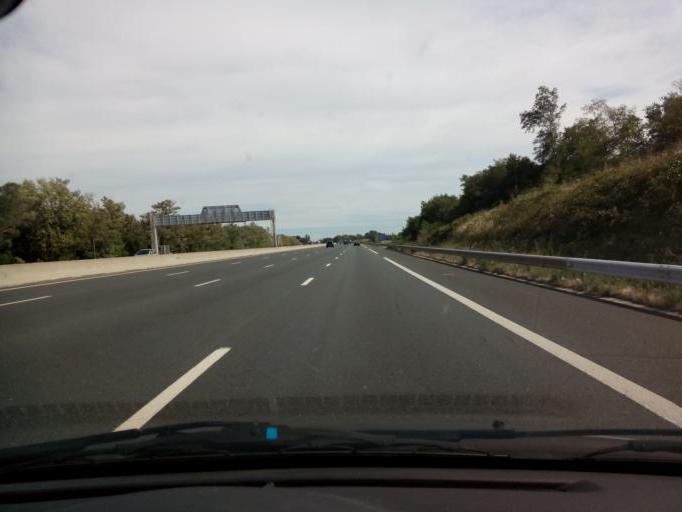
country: FR
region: Rhone-Alpes
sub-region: Departement du Rhone
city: Saint-Bonnet-de-Mure
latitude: 45.6932
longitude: 4.9849
